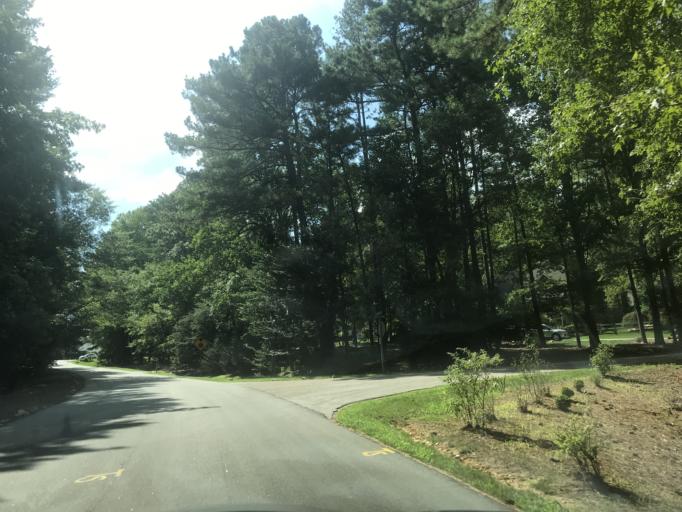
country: US
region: North Carolina
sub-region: Wake County
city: Cary
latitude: 35.8874
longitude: -78.7256
